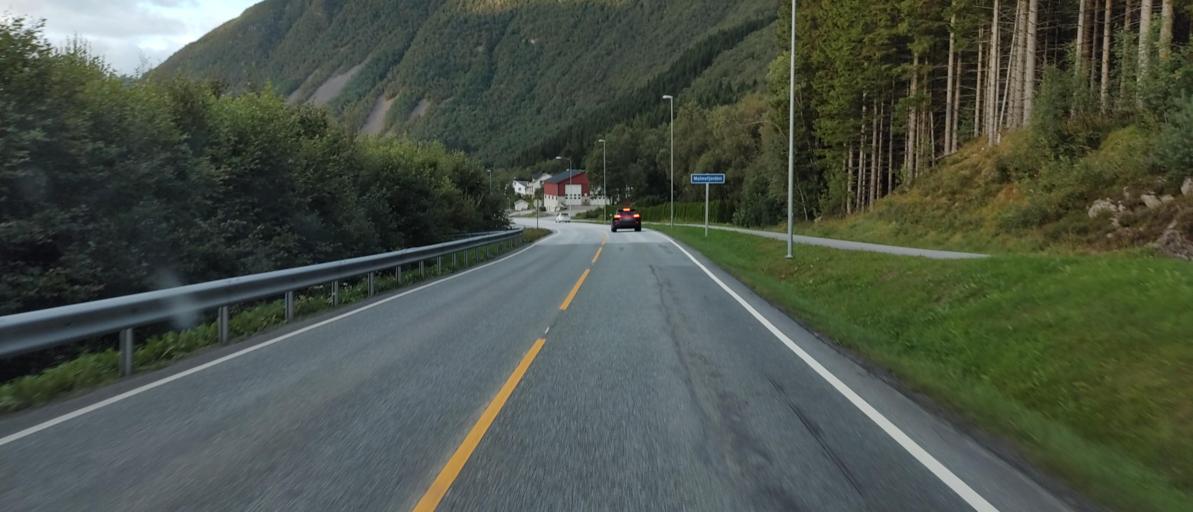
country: NO
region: More og Romsdal
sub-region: Molde
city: Molde
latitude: 62.7976
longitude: 7.2371
